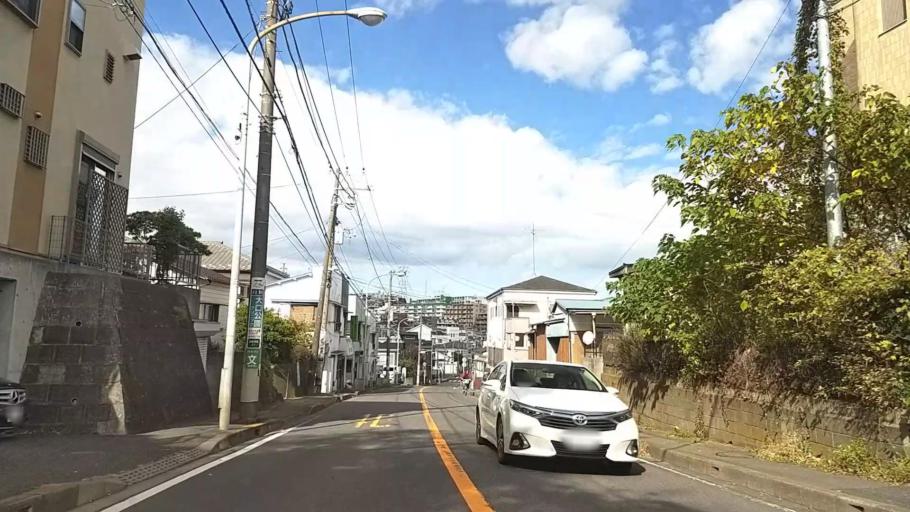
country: JP
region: Kanagawa
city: Yokohama
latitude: 35.4870
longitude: 139.6398
